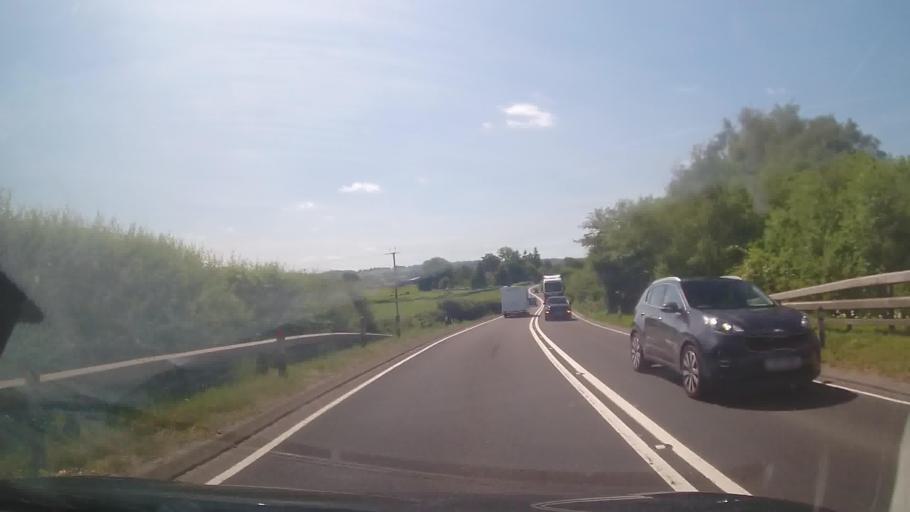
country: GB
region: England
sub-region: Herefordshire
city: Orleton
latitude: 52.3180
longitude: -2.7082
